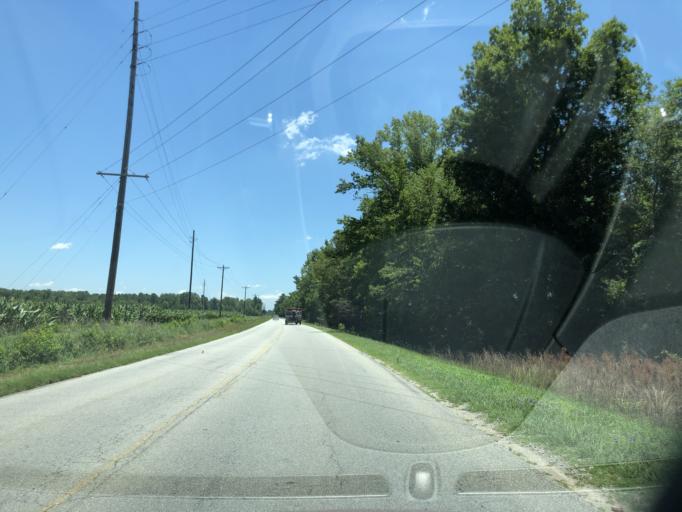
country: US
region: South Carolina
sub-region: Orangeburg County
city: Branchville
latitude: 33.2483
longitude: -80.8030
